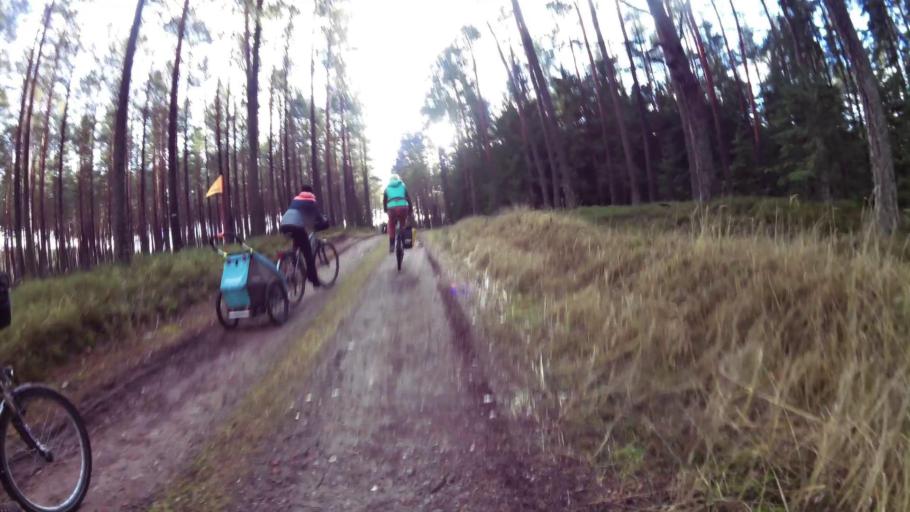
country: PL
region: West Pomeranian Voivodeship
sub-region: Powiat koszalinski
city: Sianow
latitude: 54.0901
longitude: 16.2935
